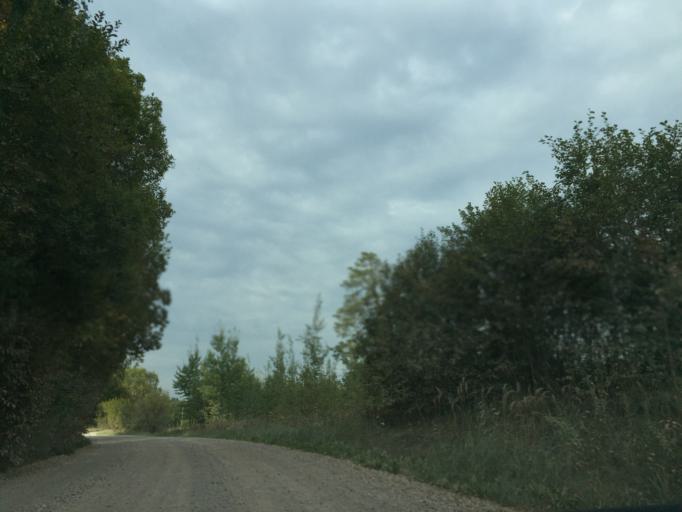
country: LV
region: Ikskile
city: Ikskile
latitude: 56.8105
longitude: 24.4472
